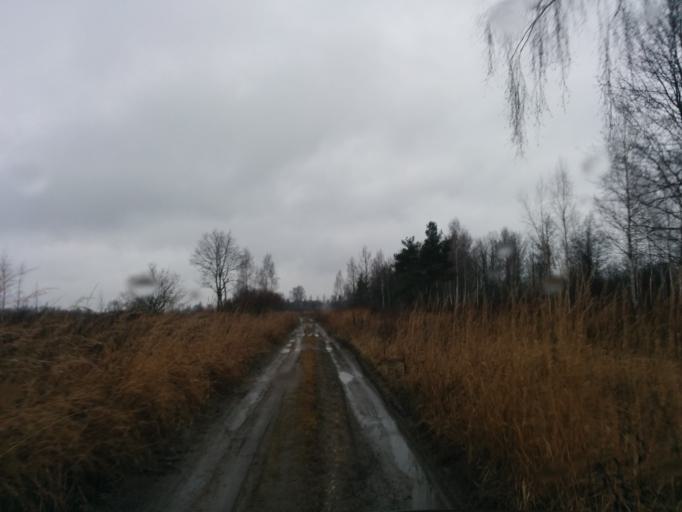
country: LV
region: Jelgava
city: Jelgava
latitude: 56.6769
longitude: 23.7101
